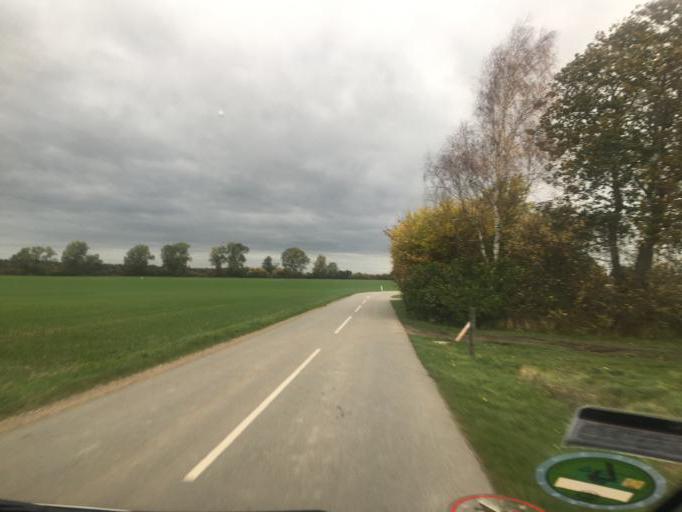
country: DK
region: Zealand
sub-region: Koge Kommune
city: Bjaeverskov
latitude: 55.4209
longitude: 11.9826
